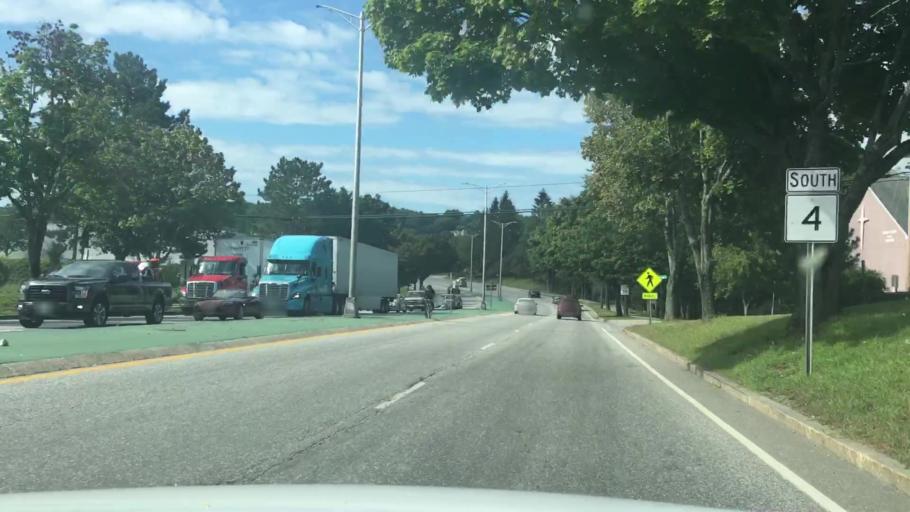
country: US
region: Maine
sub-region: Androscoggin County
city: Auburn
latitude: 44.1022
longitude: -70.2269
